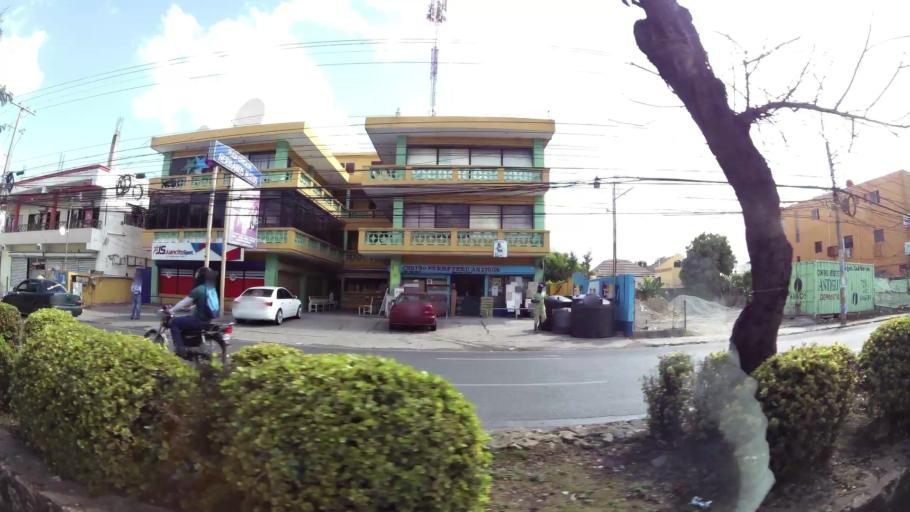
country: DO
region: Santo Domingo
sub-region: Santo Domingo
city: Santo Domingo Este
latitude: 18.5144
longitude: -69.8321
